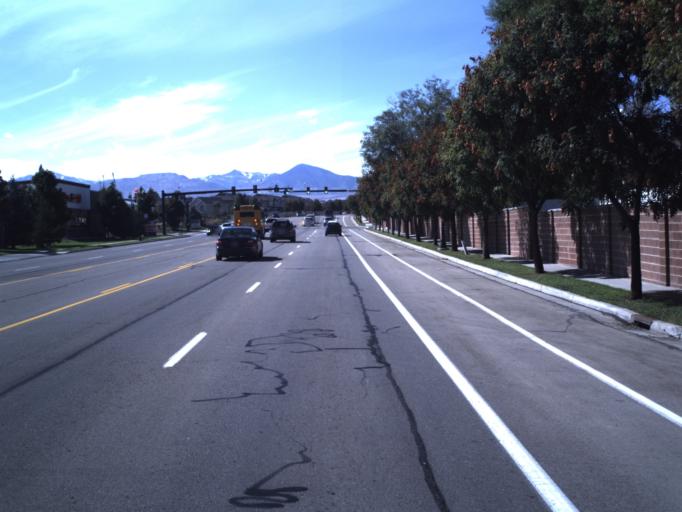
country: US
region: Utah
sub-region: Salt Lake County
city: South Jordan Heights
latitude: 40.5620
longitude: -111.9792
